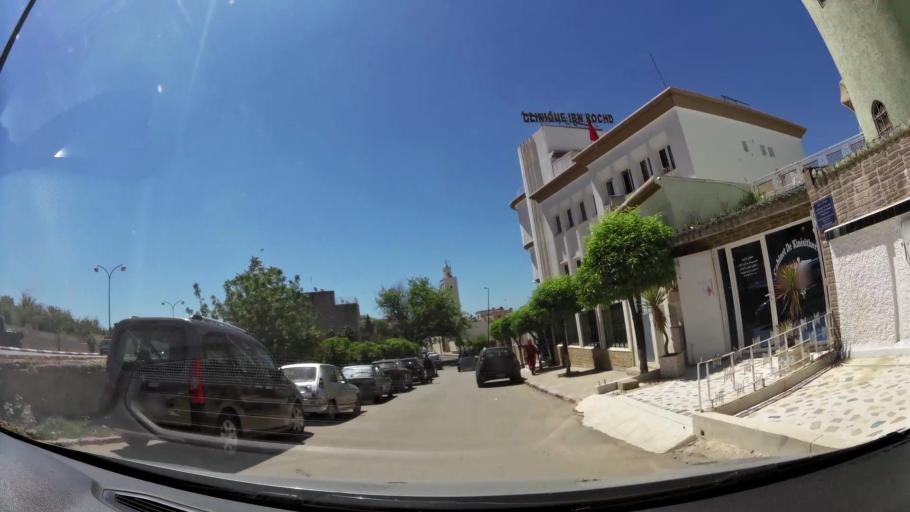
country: MA
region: Meknes-Tafilalet
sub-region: Meknes
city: Meknes
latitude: 33.8916
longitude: -5.5469
